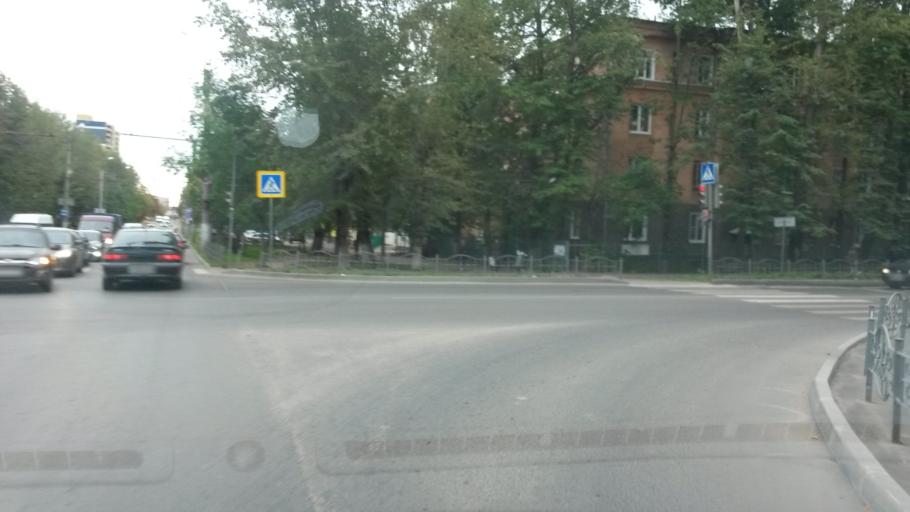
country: RU
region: Ivanovo
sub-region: Gorod Ivanovo
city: Ivanovo
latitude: 57.0193
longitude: 40.9586
